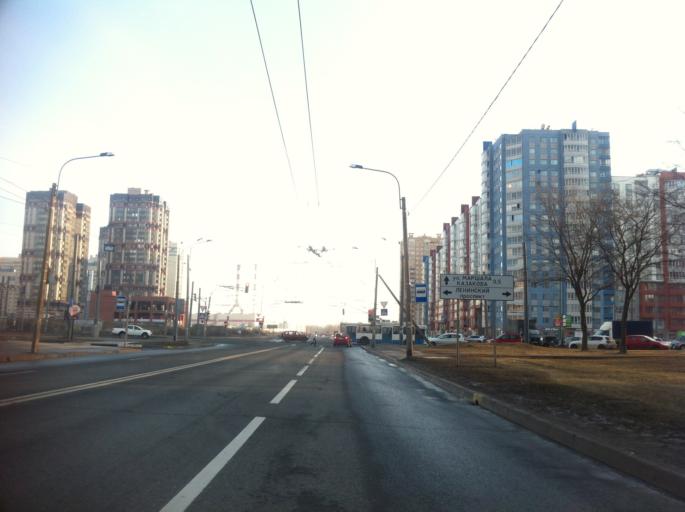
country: RU
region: St.-Petersburg
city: Uritsk
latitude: 59.8605
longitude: 30.1790
